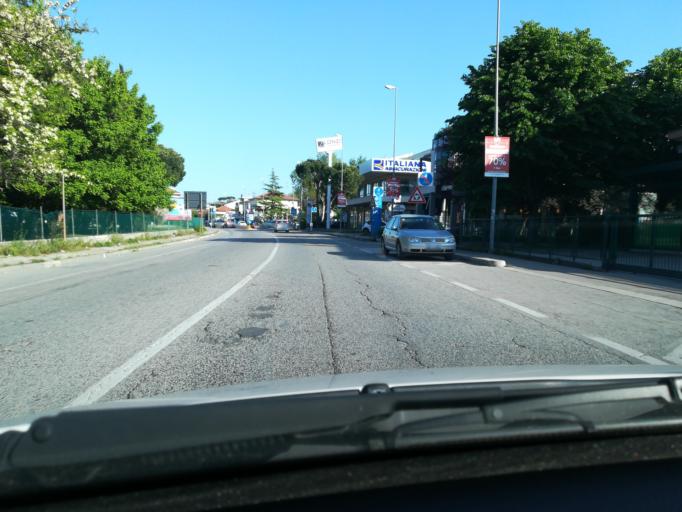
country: IT
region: Emilia-Romagna
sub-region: Provincia di Rimini
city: Riccione
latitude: 43.9940
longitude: 12.6494
